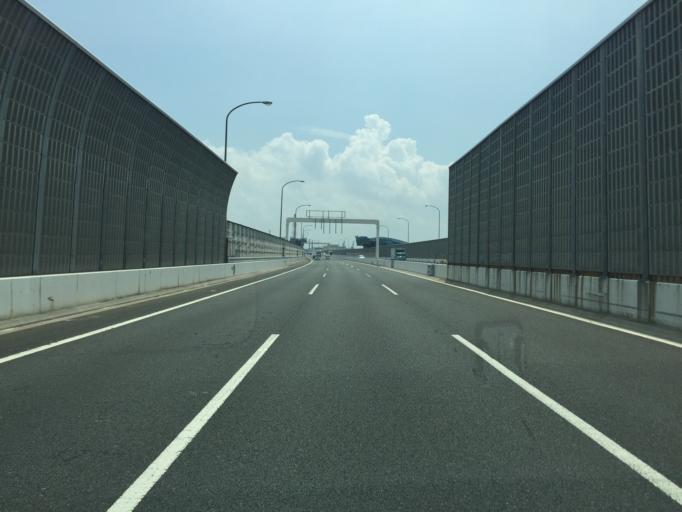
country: JP
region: Kanagawa
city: Yokohama
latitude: 35.4266
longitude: 139.6711
